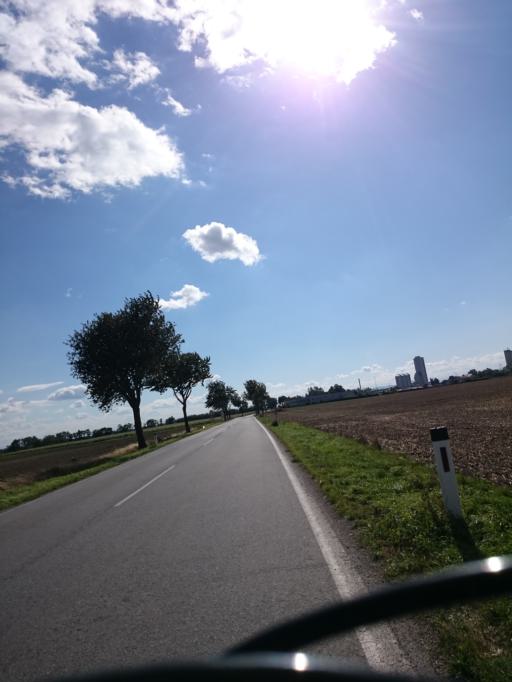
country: AT
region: Lower Austria
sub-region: Politischer Bezirk Ganserndorf
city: Grosshofen
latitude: 48.2446
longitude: 16.5969
